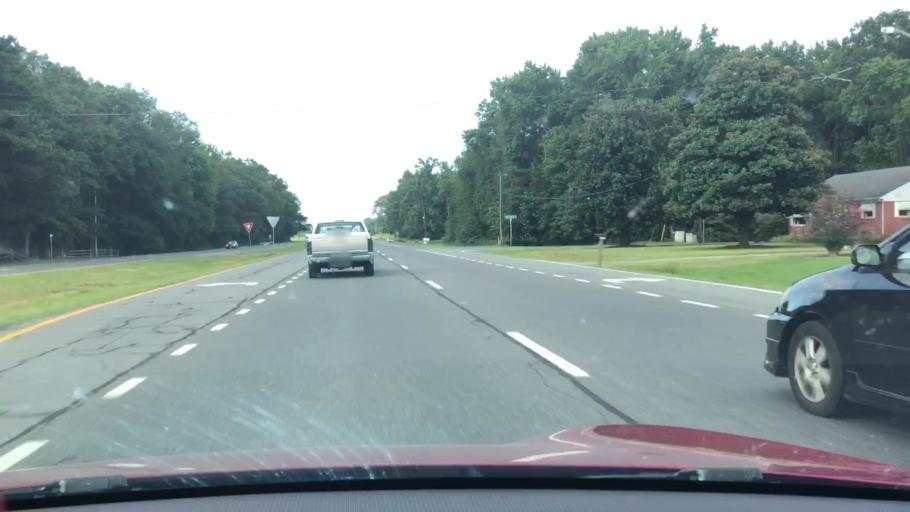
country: US
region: Delaware
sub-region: Kent County
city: Harrington
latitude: 38.8442
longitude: -75.5801
